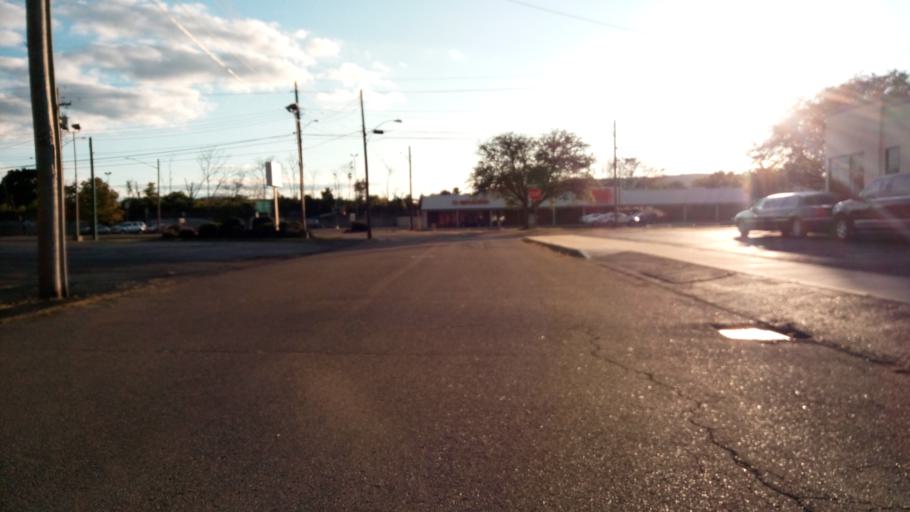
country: US
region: New York
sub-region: Chemung County
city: Elmira
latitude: 42.1011
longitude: -76.8034
